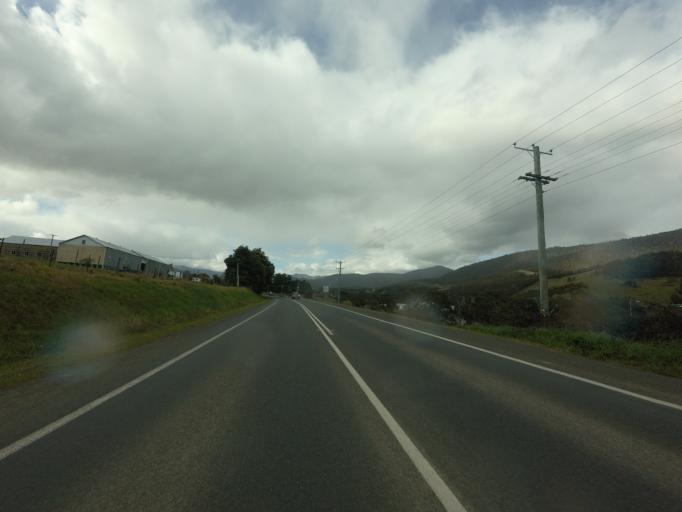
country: AU
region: Tasmania
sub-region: Huon Valley
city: Huonville
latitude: -43.0452
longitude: 147.0425
